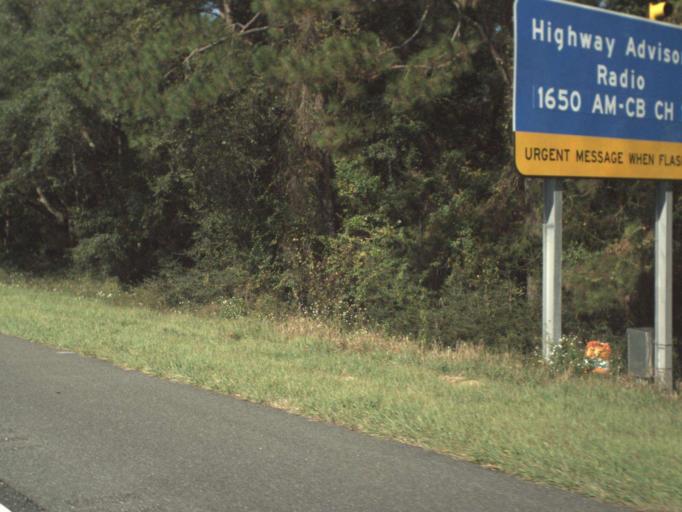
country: US
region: Florida
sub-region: Walton County
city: DeFuniak Springs
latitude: 30.7271
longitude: -85.9044
